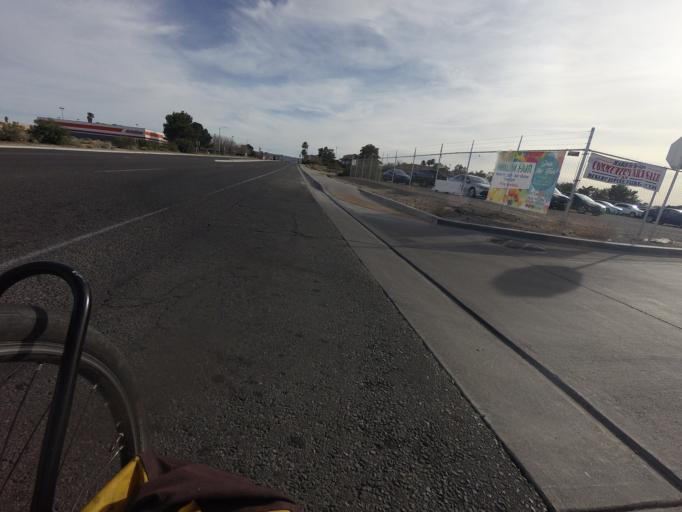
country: US
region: California
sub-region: Kern County
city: Ridgecrest
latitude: 35.6397
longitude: -117.6699
